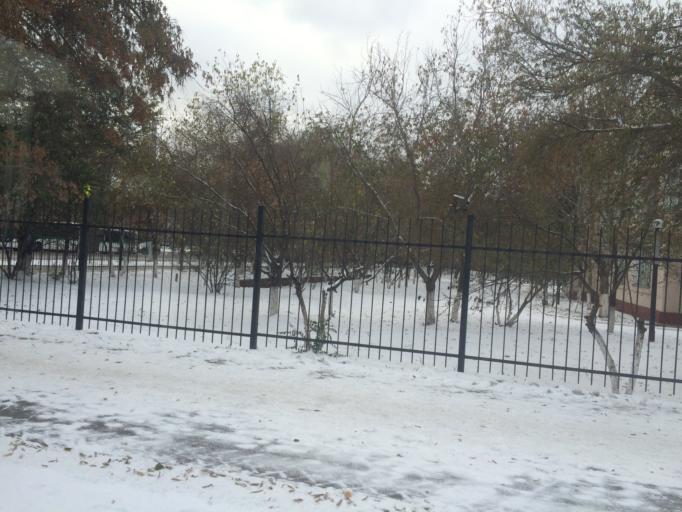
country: KZ
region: Astana Qalasy
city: Astana
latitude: 51.1712
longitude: 71.4252
